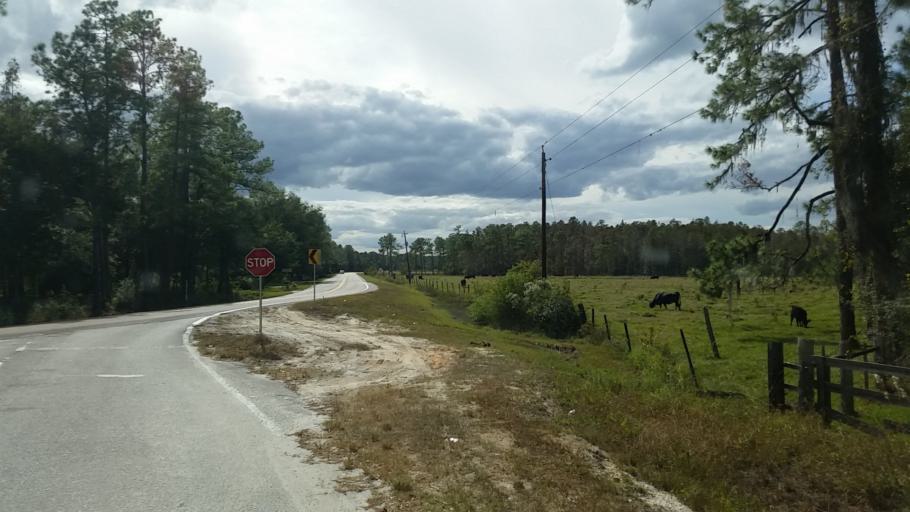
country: US
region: Florida
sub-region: Polk County
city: Gibsonia
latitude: 28.2590
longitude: -81.9584
